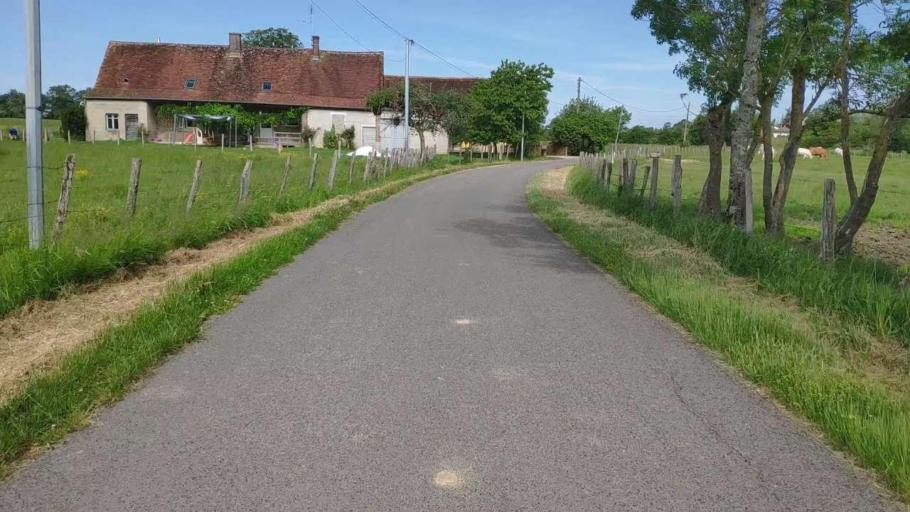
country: FR
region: Franche-Comte
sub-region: Departement du Jura
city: Bletterans
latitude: 46.6902
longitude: 5.4007
